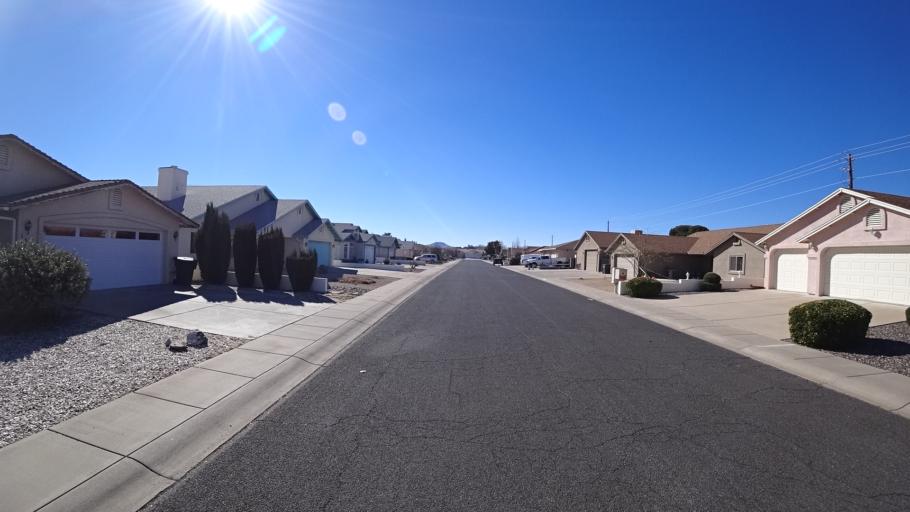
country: US
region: Arizona
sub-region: Mohave County
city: New Kingman-Butler
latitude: 35.2362
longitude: -114.0397
